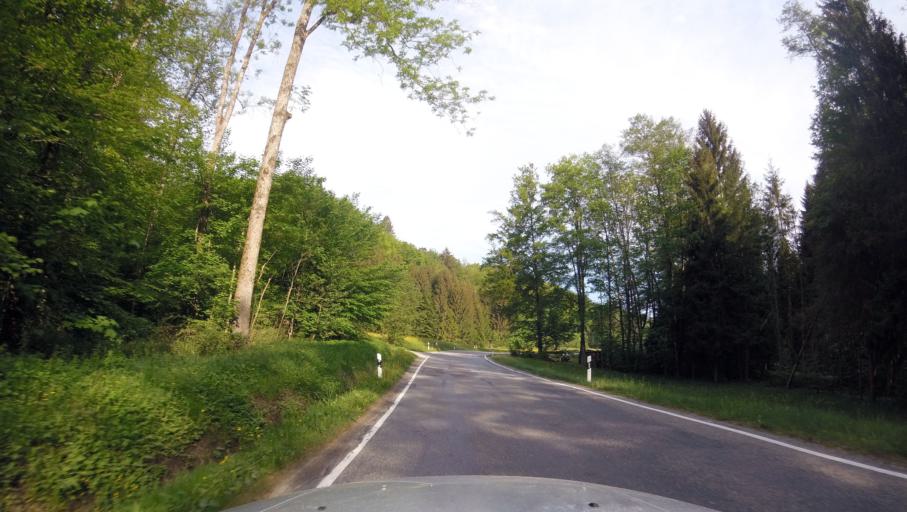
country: DE
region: Baden-Wuerttemberg
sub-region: Regierungsbezirk Stuttgart
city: Spiegelberg
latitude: 49.0651
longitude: 9.4277
